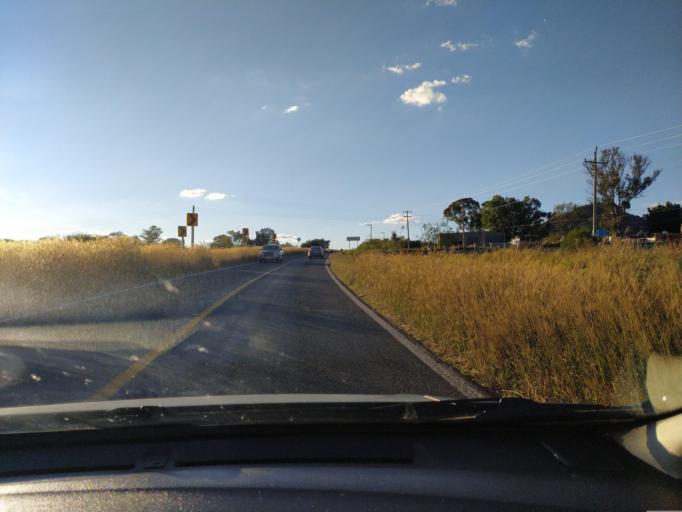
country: MX
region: Jalisco
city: San Julian
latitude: 21.0006
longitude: -102.0971
